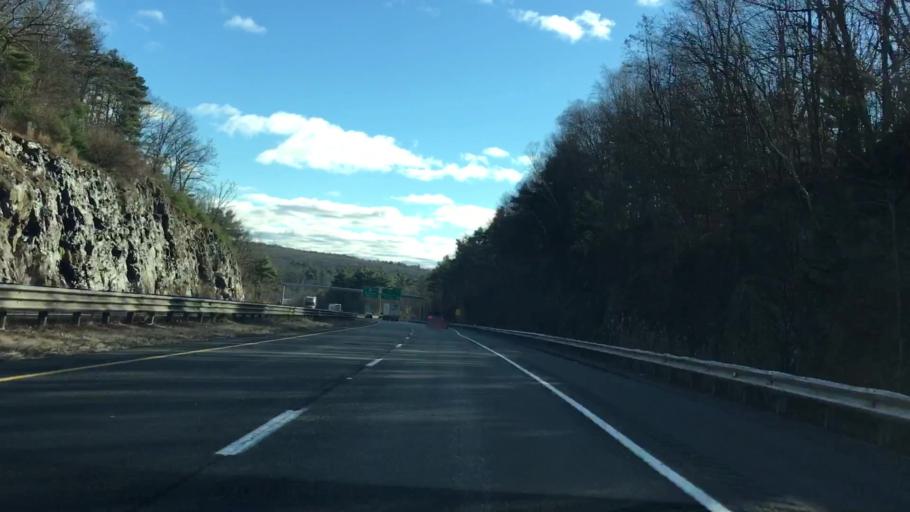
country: US
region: Massachusetts
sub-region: Worcester County
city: Sturbridge
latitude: 42.1307
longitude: -72.0704
